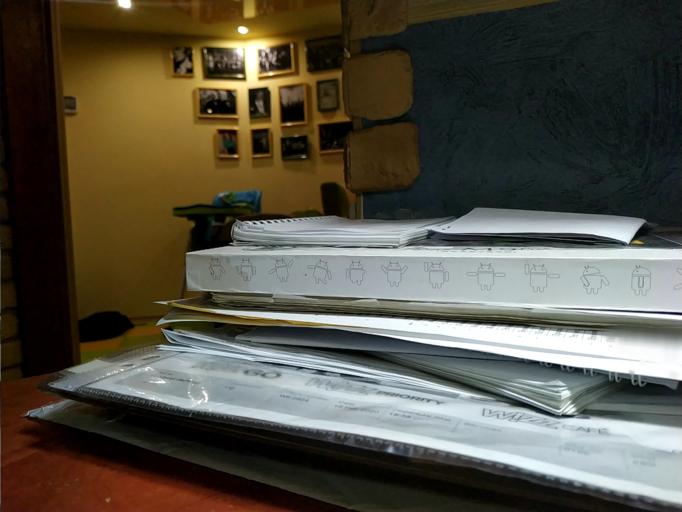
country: RU
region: Arkhangelskaya
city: Kargopol'
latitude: 61.5730
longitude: 39.2803
